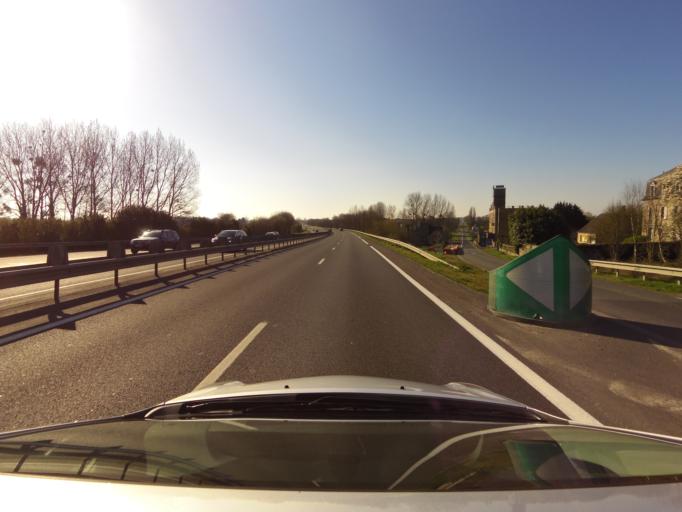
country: FR
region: Lower Normandy
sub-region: Departement de la Manche
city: Saint-Martin-des-Champs
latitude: 48.6528
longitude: -1.3529
